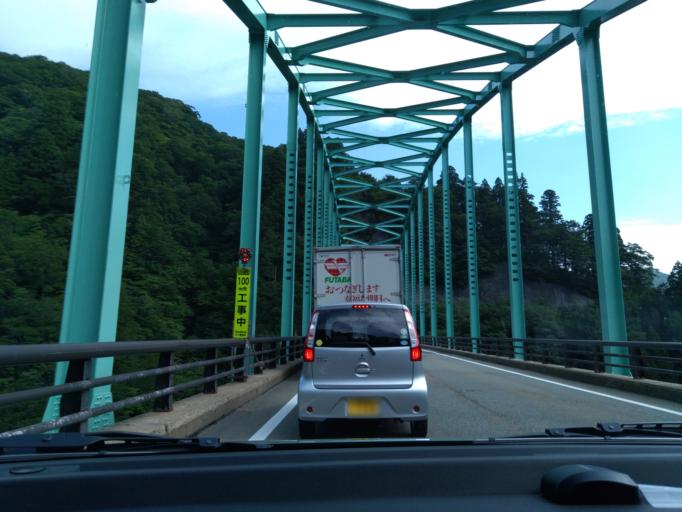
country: JP
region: Iwate
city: Shizukuishi
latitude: 39.6969
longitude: 140.7763
